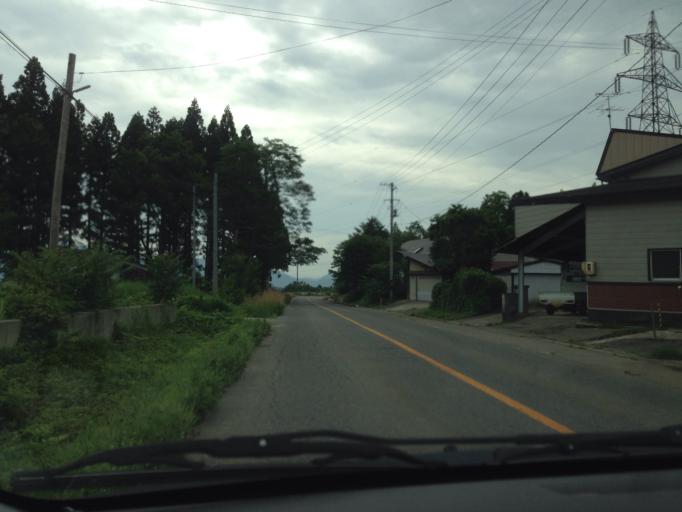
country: JP
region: Fukushima
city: Inawashiro
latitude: 37.5489
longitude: 140.0579
